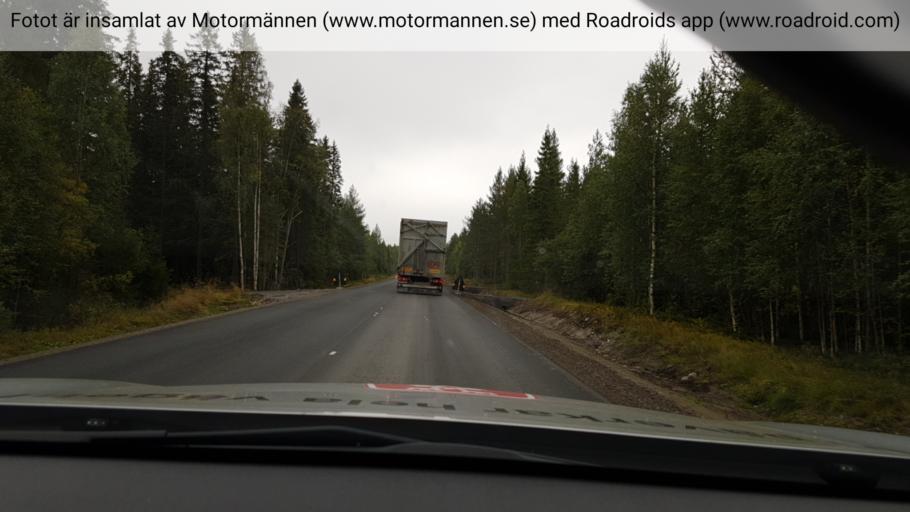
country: SE
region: Vaesterbotten
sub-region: Skelleftea Kommun
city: Burtraesk
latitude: 64.3994
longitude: 20.5488
